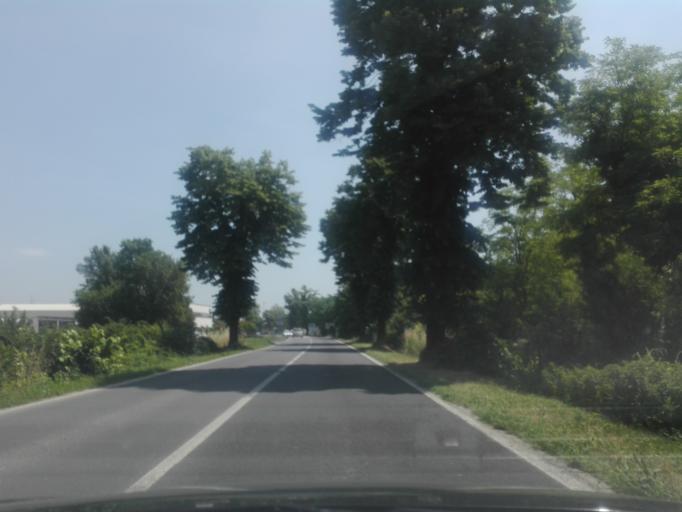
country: IT
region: Veneto
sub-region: Provincia di Rovigo
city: Adria
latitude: 45.0610
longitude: 12.0432
